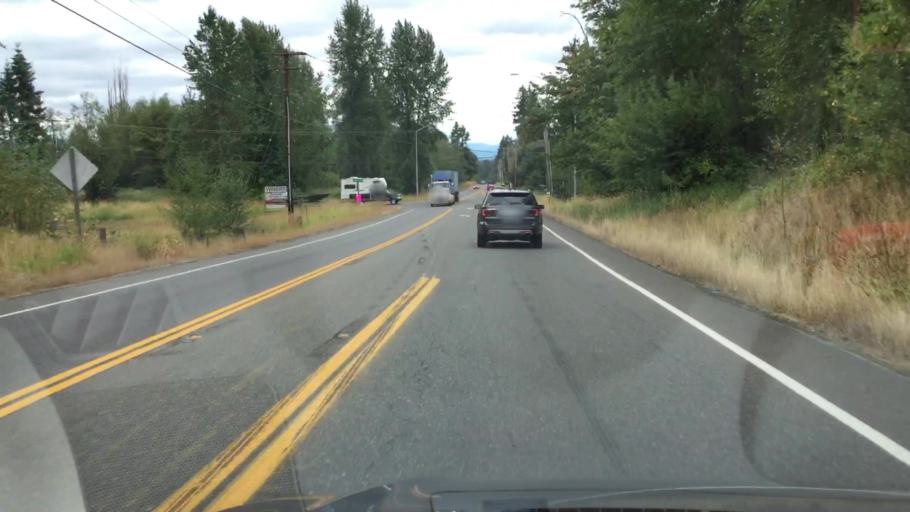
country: US
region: Washington
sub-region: Pierce County
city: Graham
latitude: 47.0177
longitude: -122.2963
